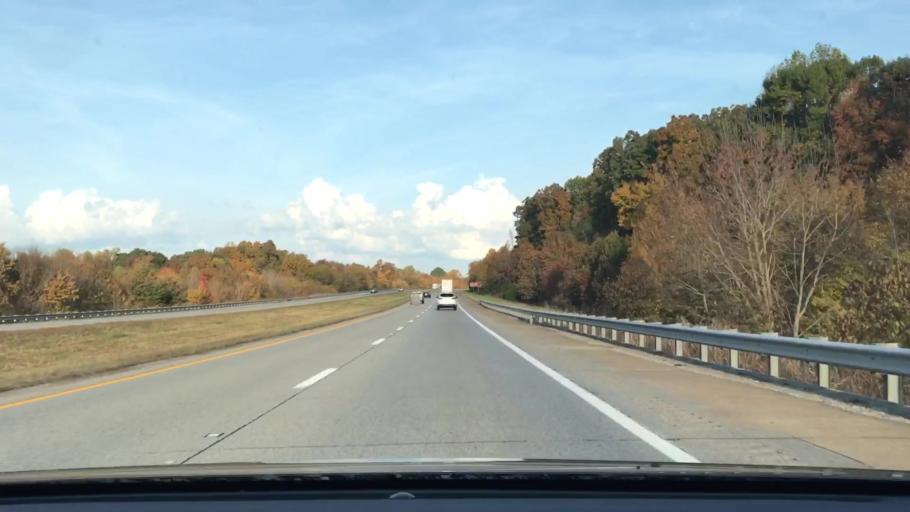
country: US
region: Kentucky
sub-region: Lyon County
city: Eddyville
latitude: 37.0261
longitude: -87.9945
